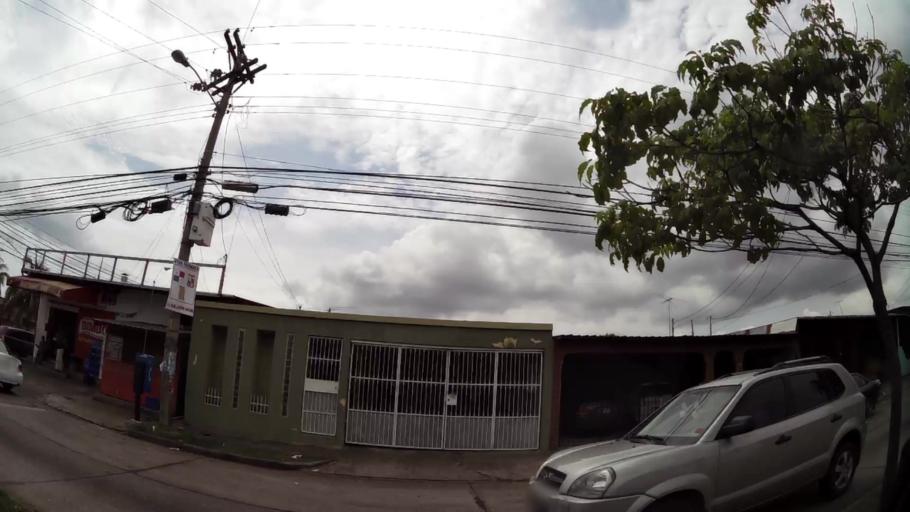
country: PA
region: Panama
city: San Miguelito
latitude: 9.0506
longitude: -79.4206
